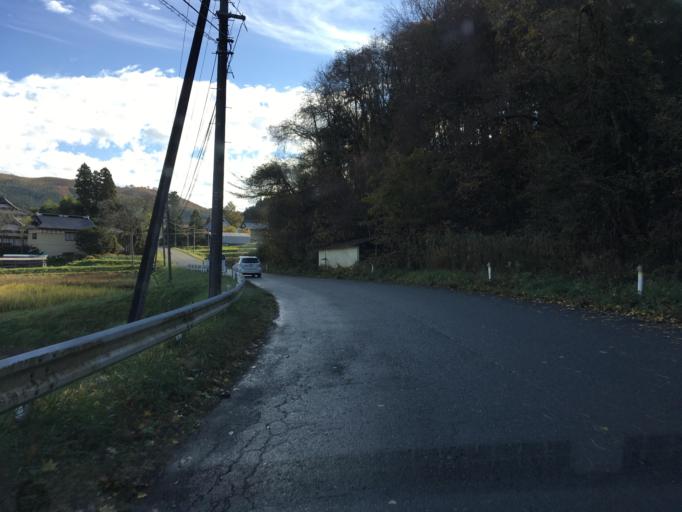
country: JP
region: Iwate
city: Ichinoseki
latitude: 38.8932
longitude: 141.4436
